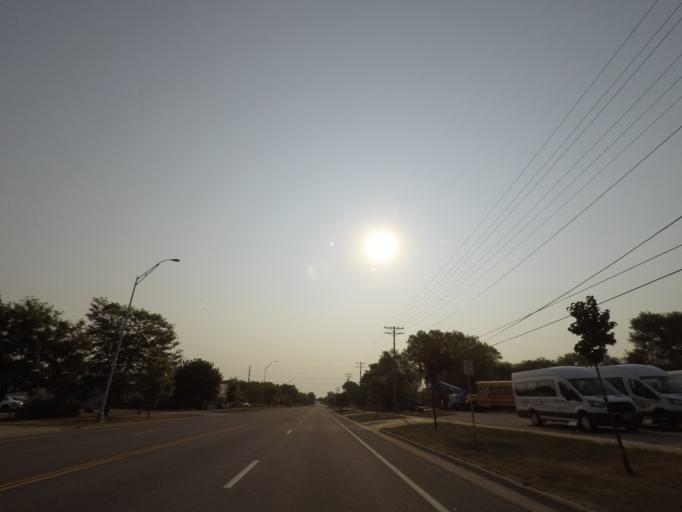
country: US
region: Wisconsin
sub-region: Dane County
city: McFarland
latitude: 43.0517
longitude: -89.2857
